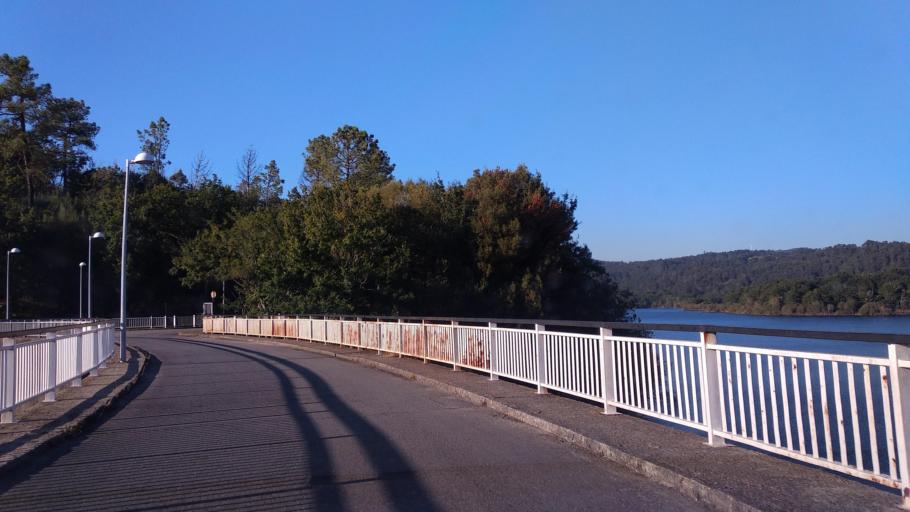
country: ES
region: Galicia
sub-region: Provincia de Pontevedra
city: Fornelos de Montes
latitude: 42.3466
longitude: -8.4896
